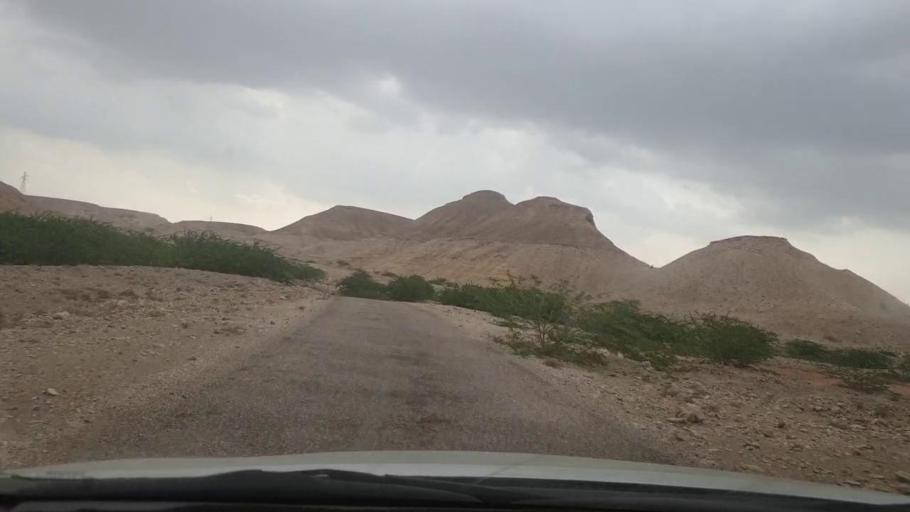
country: PK
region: Sindh
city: Khairpur
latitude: 27.4709
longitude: 68.9134
